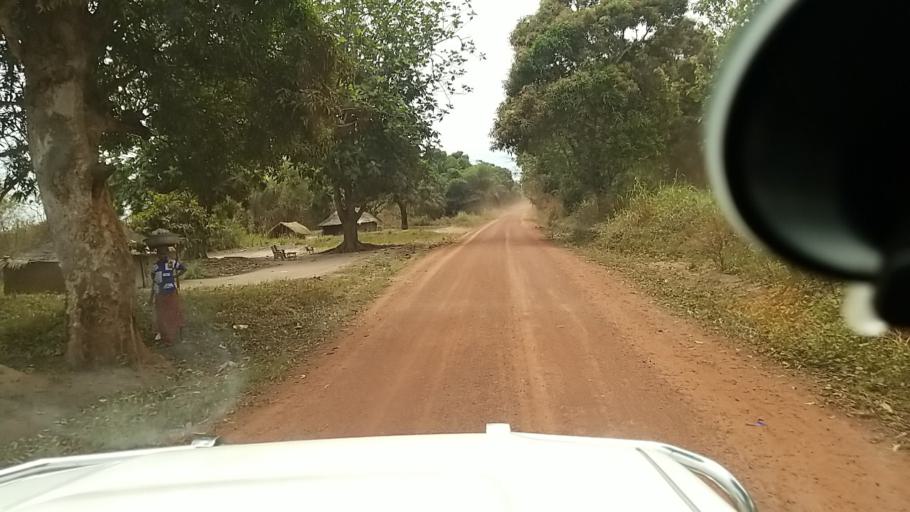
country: CD
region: Equateur
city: Libenge
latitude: 3.7407
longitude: 18.7819
